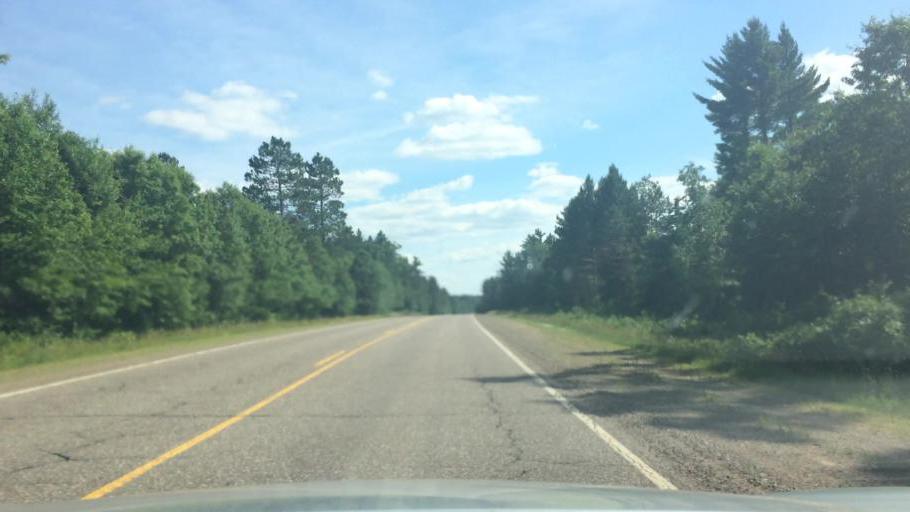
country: US
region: Wisconsin
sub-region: Vilas County
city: Lac du Flambeau
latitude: 46.0750
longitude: -89.6442
